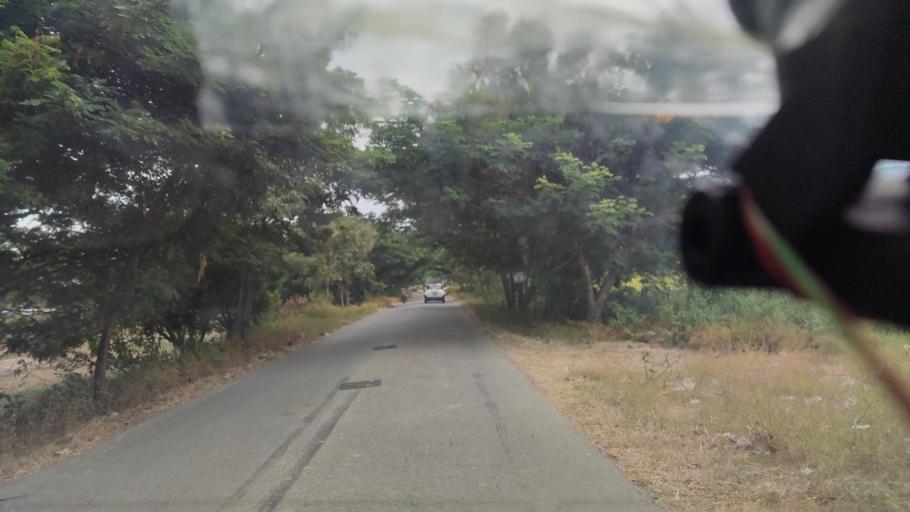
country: MM
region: Mandalay
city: Pyinmana
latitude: 19.7573
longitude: 96.3060
